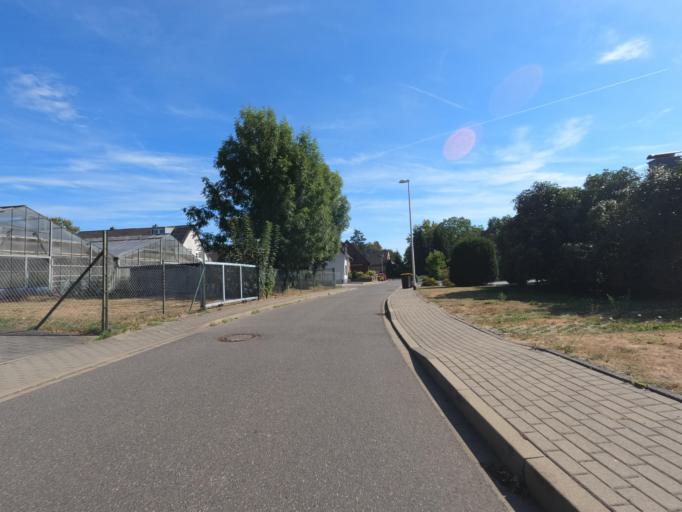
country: DE
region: North Rhine-Westphalia
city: Erkelenz
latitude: 51.0336
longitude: 6.3594
